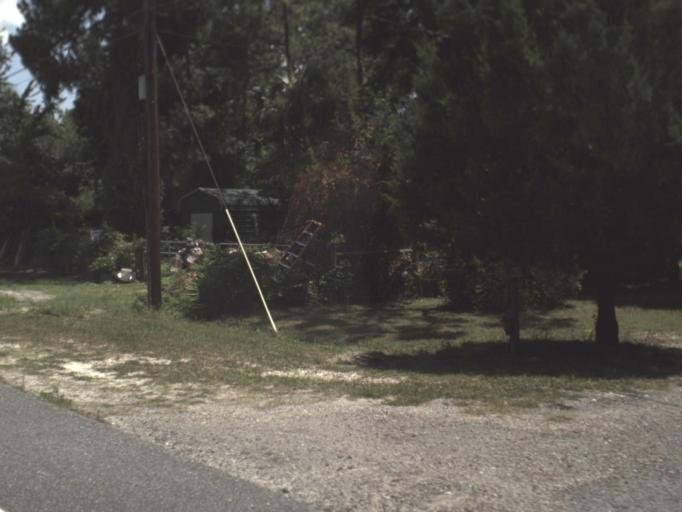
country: US
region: Florida
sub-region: Taylor County
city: Steinhatchee
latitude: 29.6939
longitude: -83.3564
